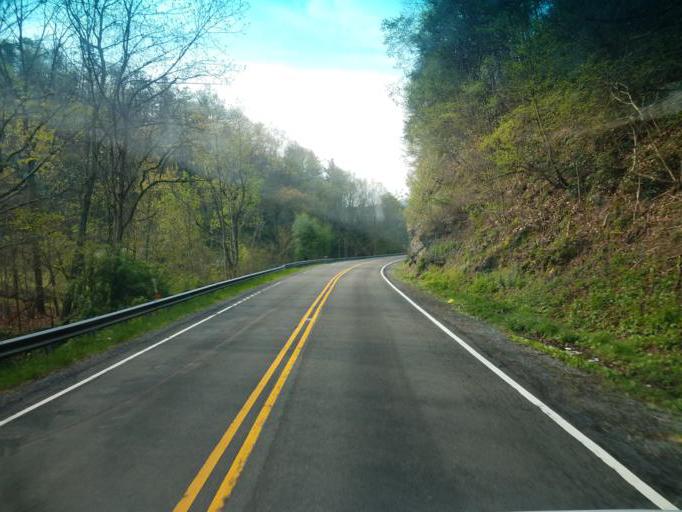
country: US
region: Virginia
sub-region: Smyth County
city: Atkins
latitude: 36.7991
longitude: -81.4035
